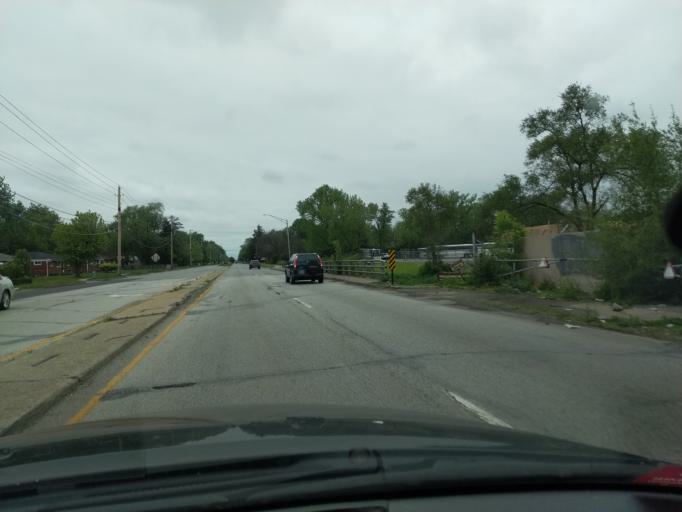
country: US
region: Indiana
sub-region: Marion County
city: Lawrence
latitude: 39.8259
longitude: -86.0648
